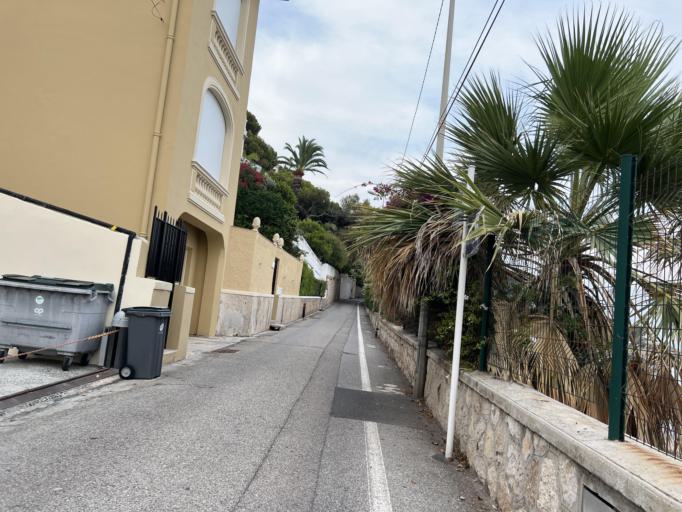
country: FR
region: Provence-Alpes-Cote d'Azur
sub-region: Departement des Alpes-Maritimes
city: Cap-d'Ail
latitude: 43.7201
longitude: 7.3902
